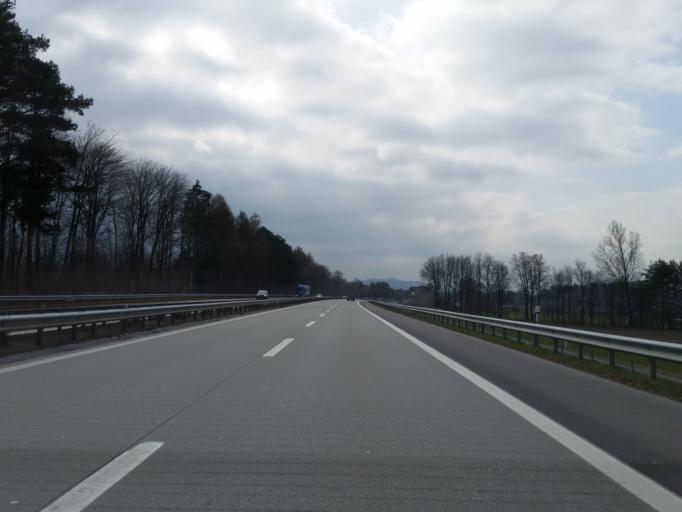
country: CH
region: Saint Gallen
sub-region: Wahlkreis Rheintal
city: Ruthi
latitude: 47.2933
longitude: 9.5517
